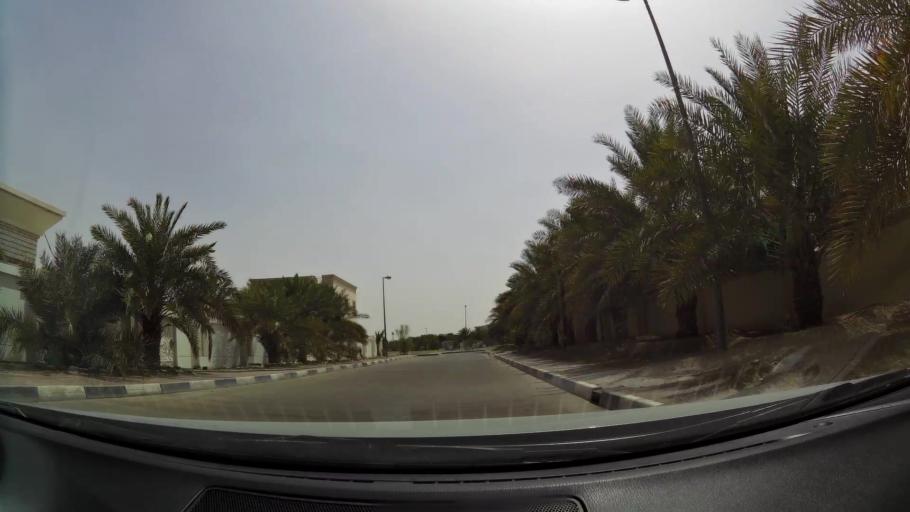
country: AE
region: Abu Dhabi
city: Al Ain
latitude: 24.1624
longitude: 55.6616
